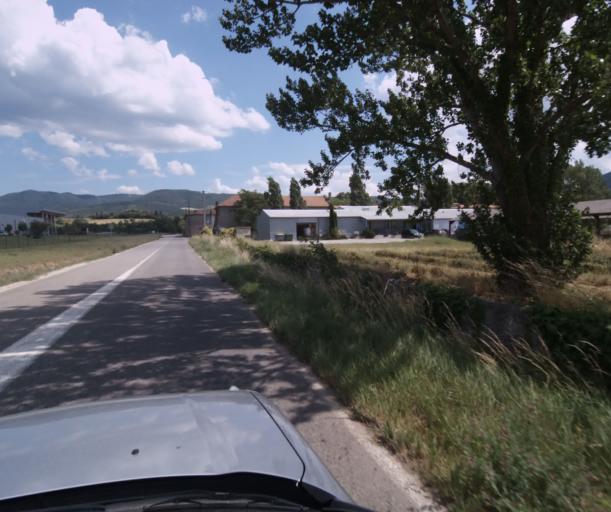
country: FR
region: Languedoc-Roussillon
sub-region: Departement de l'Aude
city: Limoux
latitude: 43.0425
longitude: 2.2463
